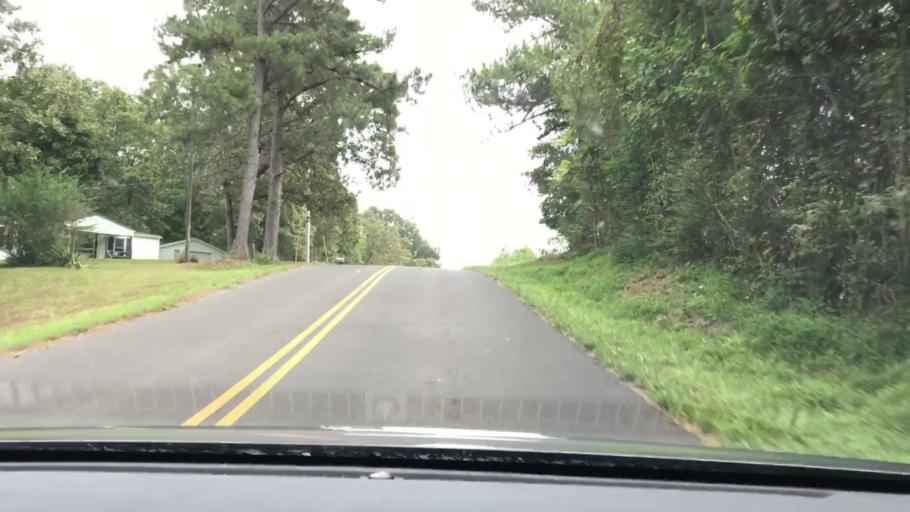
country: US
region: Kentucky
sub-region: Marshall County
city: Benton
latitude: 36.8317
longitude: -88.3656
